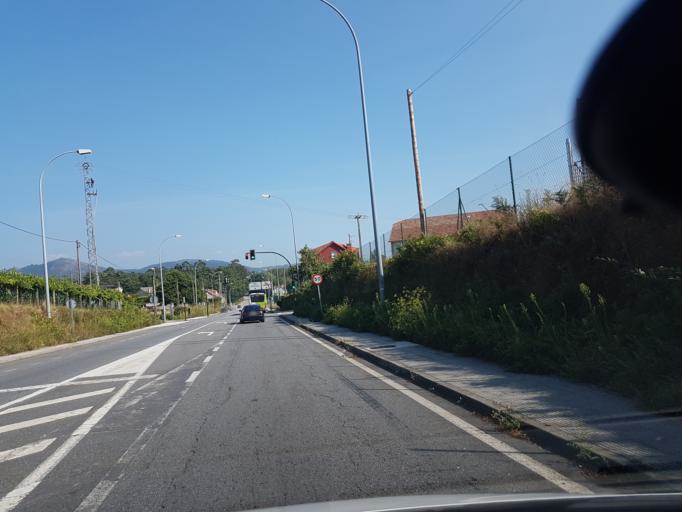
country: ES
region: Galicia
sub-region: Provincia de Pontevedra
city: Redondela
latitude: 42.2319
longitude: -8.6406
